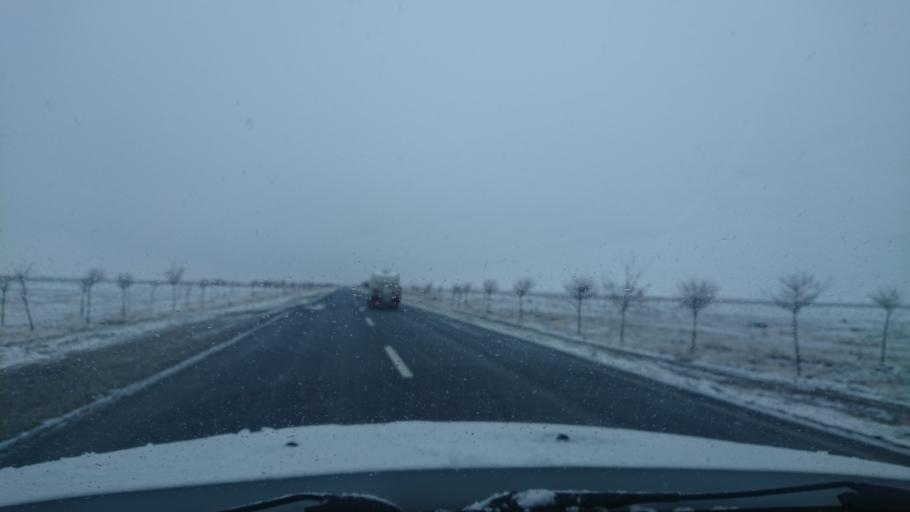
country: TR
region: Aksaray
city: Yesilova
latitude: 38.3133
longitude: 33.7536
